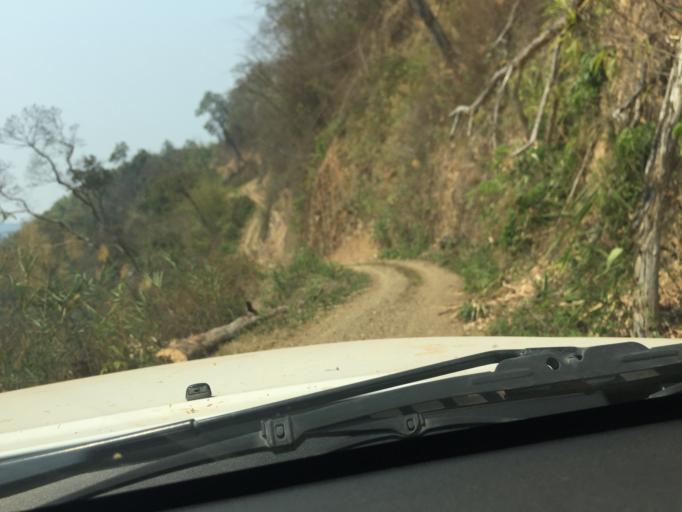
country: LA
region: Loungnamtha
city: Muang Nale
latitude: 20.6187
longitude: 101.6117
